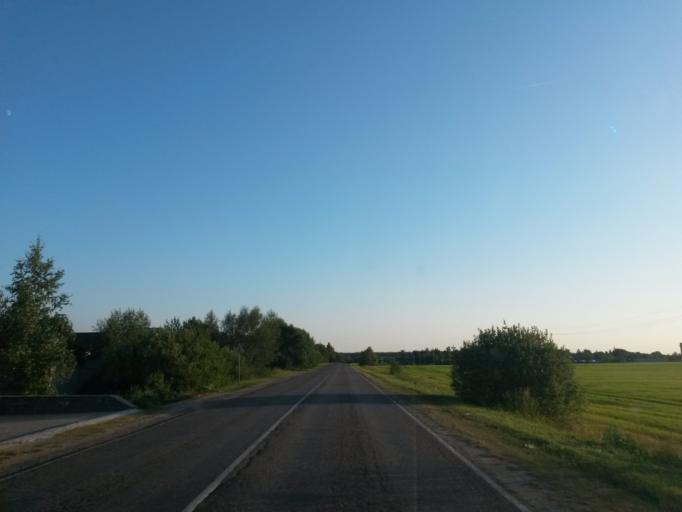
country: RU
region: Moskovskaya
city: Belyye Stolby
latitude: 55.2904
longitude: 37.7855
